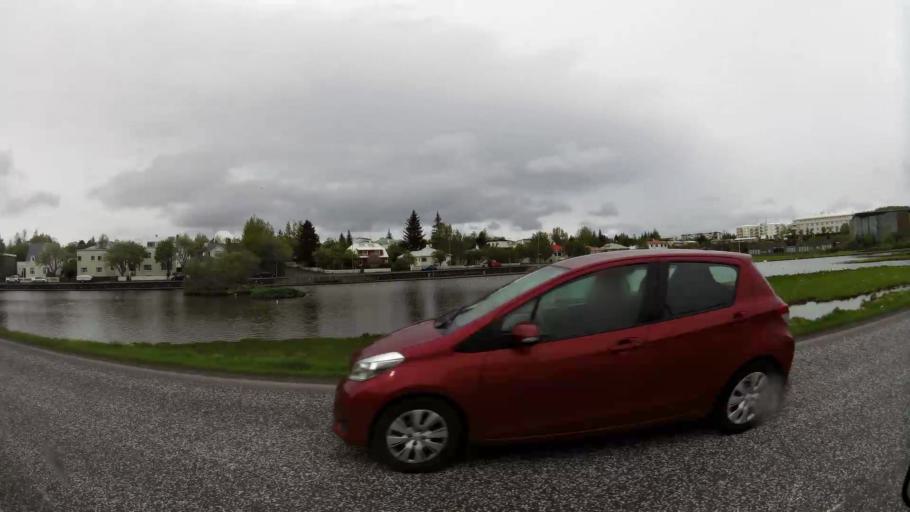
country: IS
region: Capital Region
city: Hafnarfjoerdur
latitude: 64.0672
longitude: -21.9459
